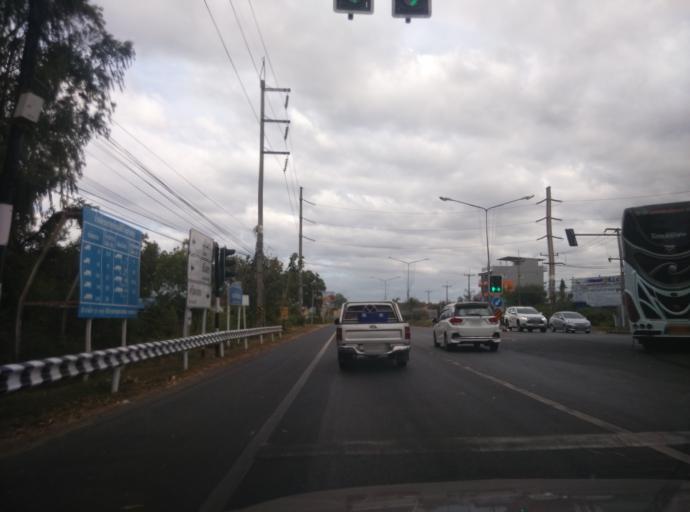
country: TH
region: Sisaket
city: Si Sa Ket
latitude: 15.1265
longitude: 104.2844
